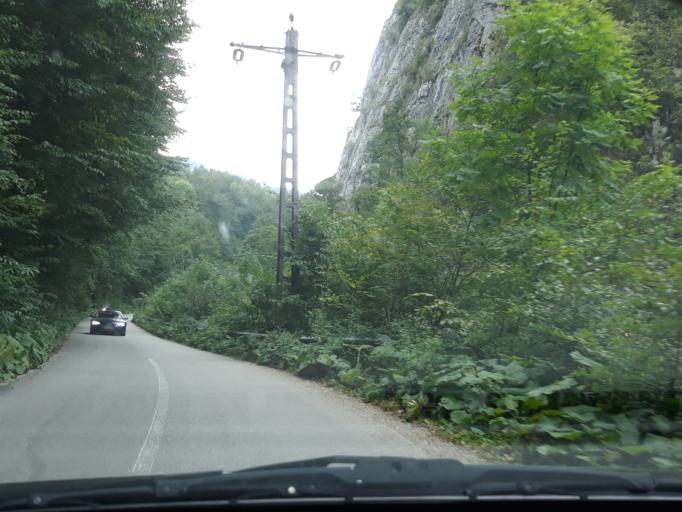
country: RO
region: Bihor
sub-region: Comuna Pietroasa
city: Pietroasa
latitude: 46.6029
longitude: 22.6434
